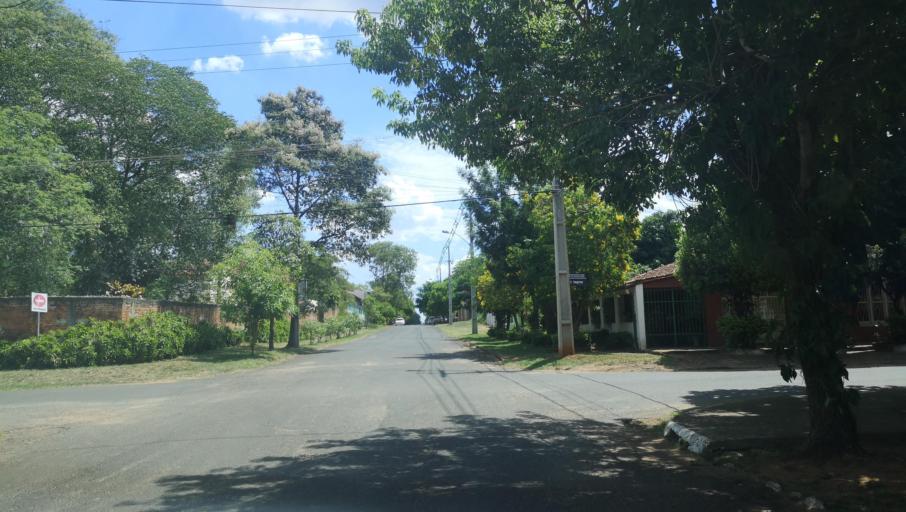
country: PY
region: Misiones
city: Santa Maria
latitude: -26.8915
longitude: -57.0221
